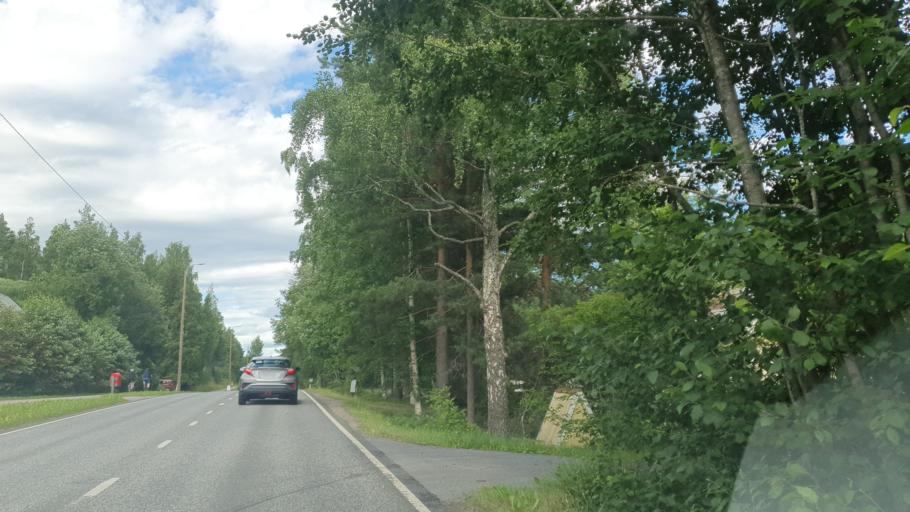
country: FI
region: Central Finland
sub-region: Jyvaeskylae
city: Saeynaetsalo
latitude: 62.1477
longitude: 25.7505
